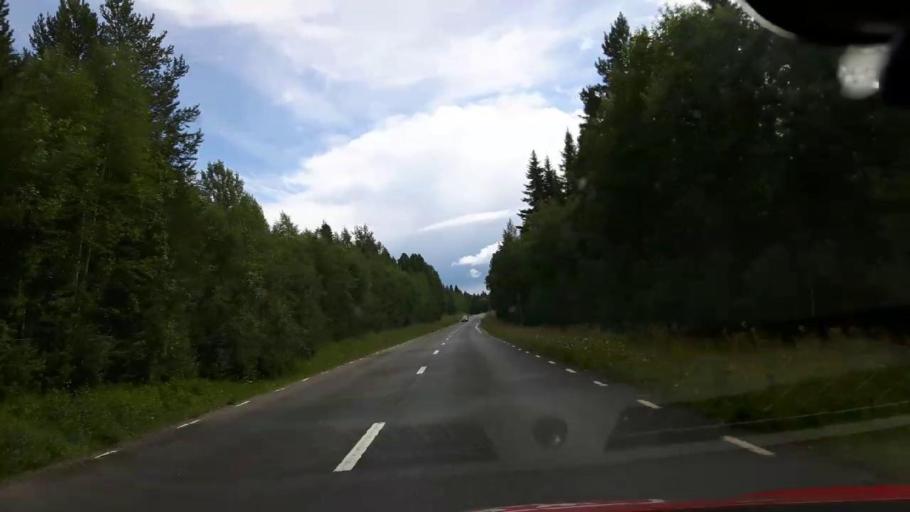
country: SE
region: Jaemtland
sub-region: Stroemsunds Kommun
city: Stroemsund
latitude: 64.3410
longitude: 14.9491
